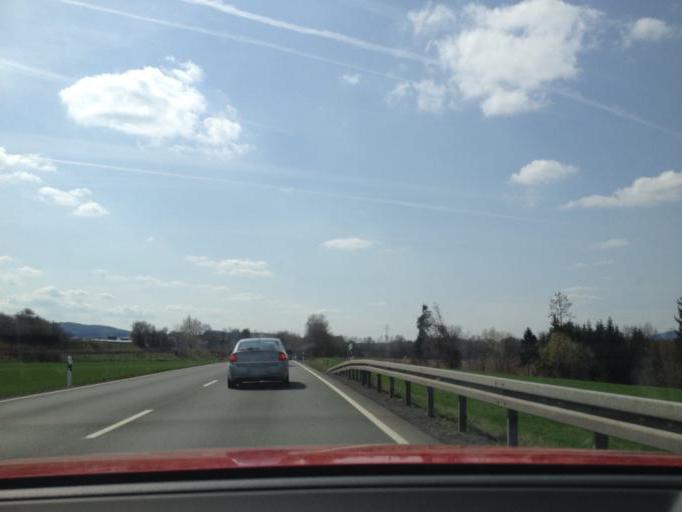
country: DE
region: Bavaria
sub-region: Upper Franconia
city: Marktredwitz
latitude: 50.0209
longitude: 12.1284
